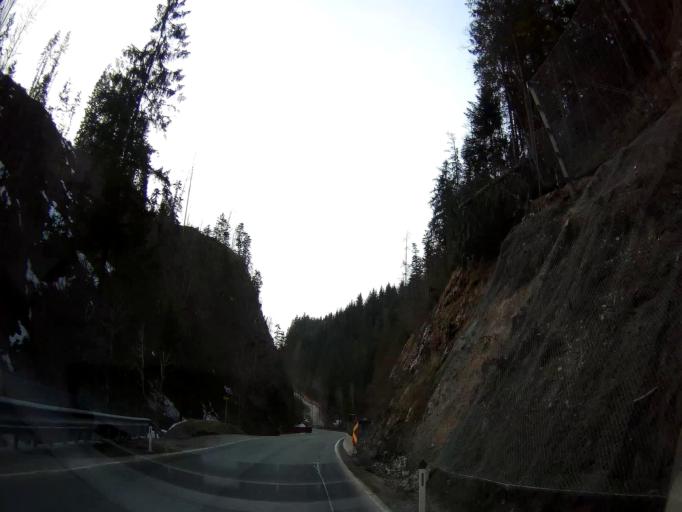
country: AT
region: Salzburg
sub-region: Politischer Bezirk Hallein
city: Abtenau
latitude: 47.5443
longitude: 13.4204
